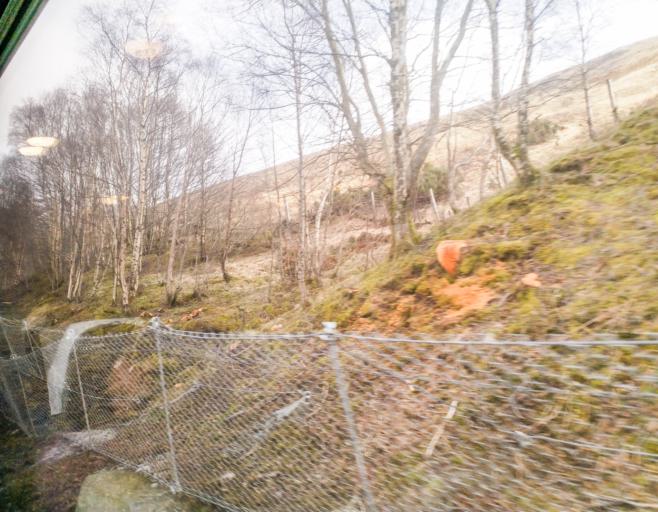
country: GB
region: Scotland
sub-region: Highland
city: Spean Bridge
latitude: 56.8023
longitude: -4.7200
